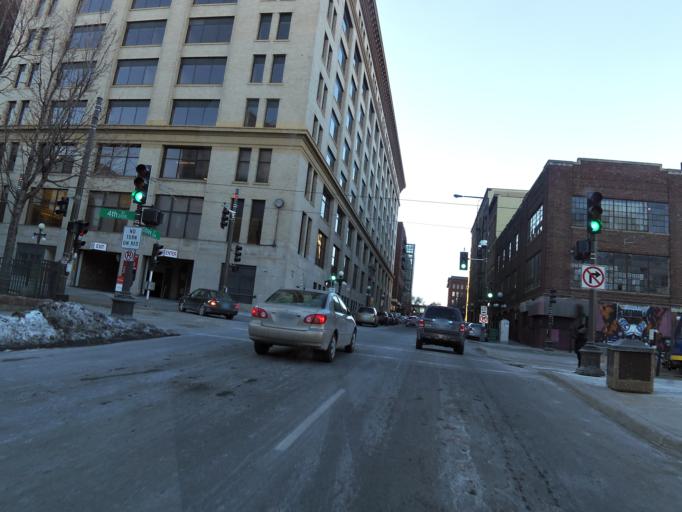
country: US
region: Minnesota
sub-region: Ramsey County
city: Saint Paul
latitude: 44.9477
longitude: -93.0874
